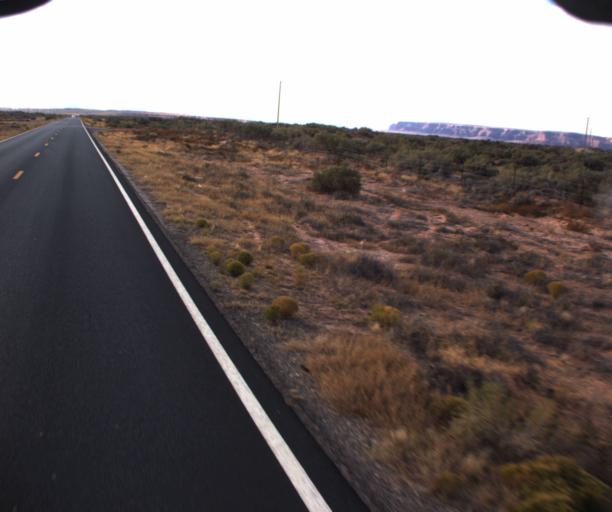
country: US
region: Arizona
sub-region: Apache County
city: Many Farms
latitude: 36.6417
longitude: -109.5890
